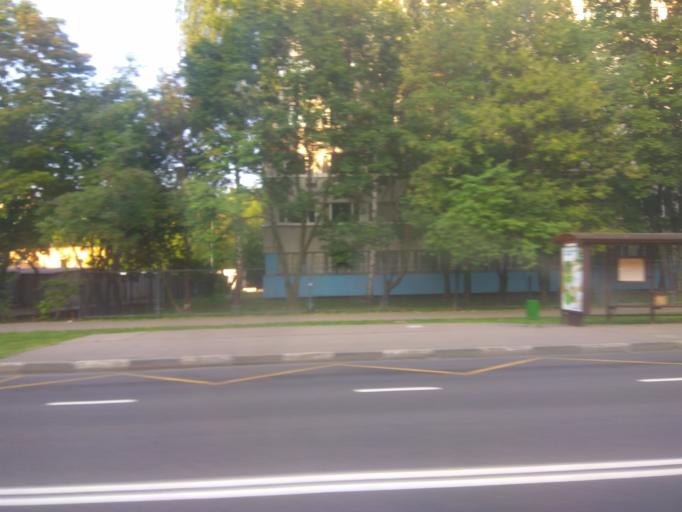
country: RU
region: Moscow
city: Orekhovo-Borisovo
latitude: 55.6124
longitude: 37.7077
